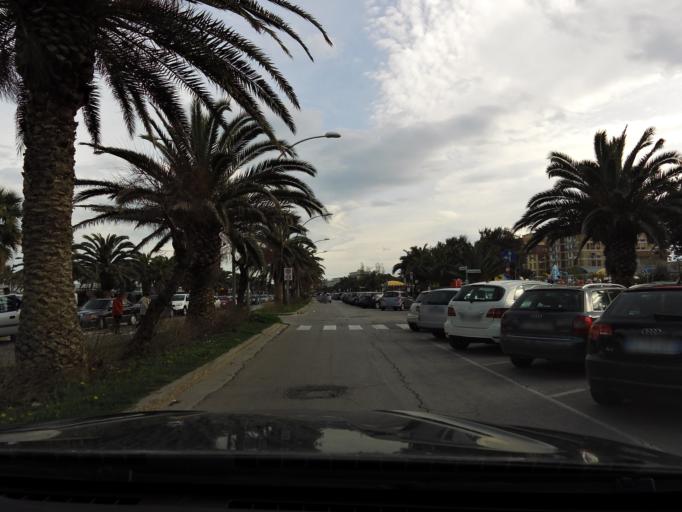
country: IT
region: The Marches
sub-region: Provincia di Macerata
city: Portocivitanova
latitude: 43.3074
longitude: 13.7339
